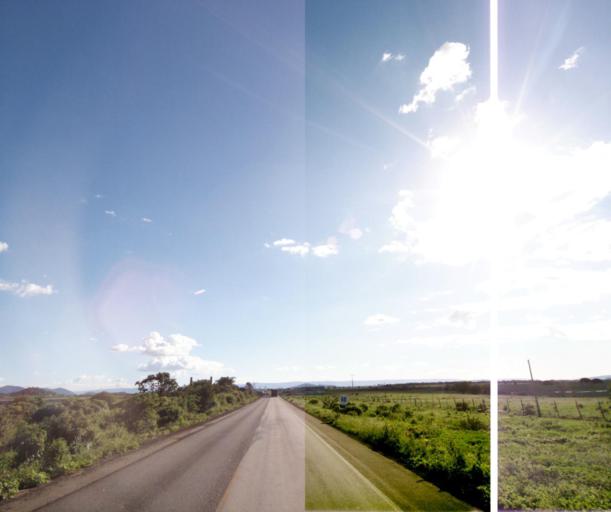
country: BR
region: Bahia
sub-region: Guanambi
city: Guanambi
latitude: -14.1794
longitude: -42.7332
